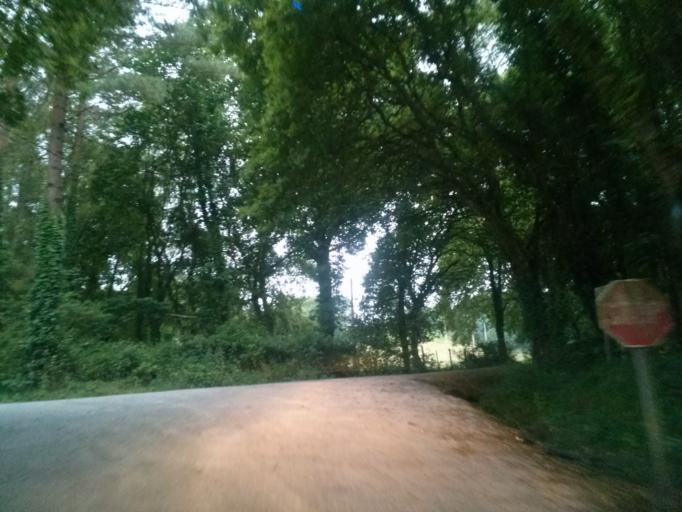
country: ES
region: Galicia
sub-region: Provincia de Lugo
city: Begonte
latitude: 43.1409
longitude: -7.7732
